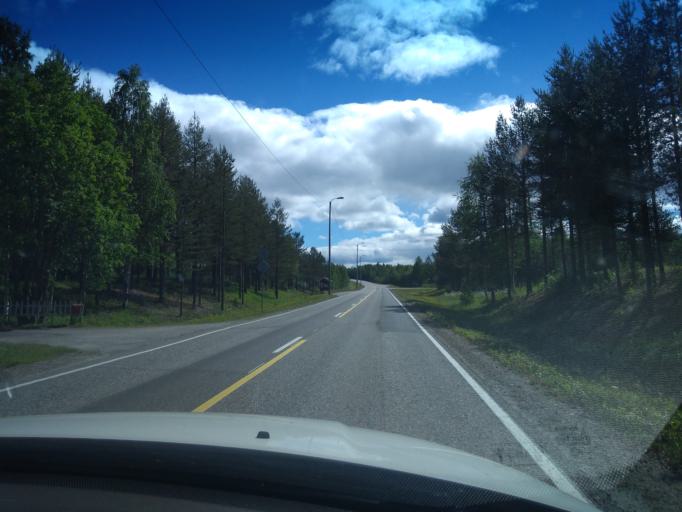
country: FI
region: Lapland
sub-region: Tunturi-Lappi
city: Kittilae
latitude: 67.2749
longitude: 24.8830
